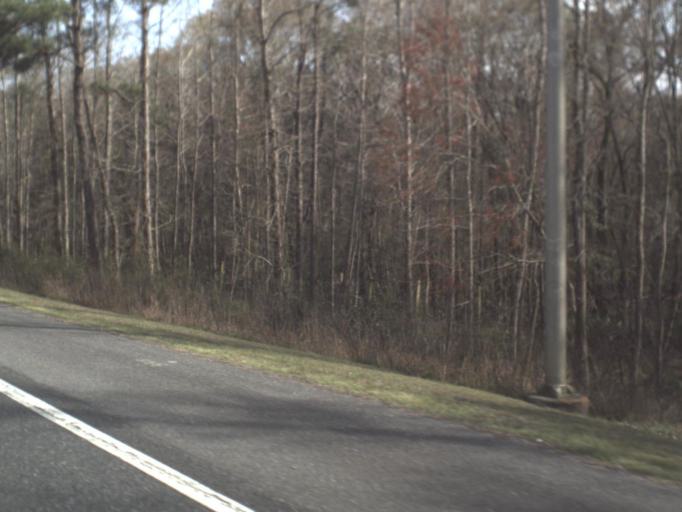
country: US
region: Florida
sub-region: Gadsden County
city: Midway
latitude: 30.4847
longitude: -84.3927
